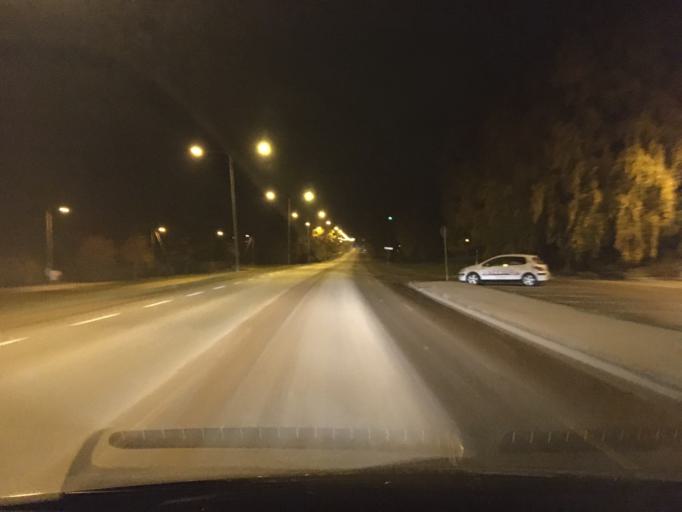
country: EE
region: Tartu
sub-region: Tartu linn
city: Tartu
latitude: 58.4001
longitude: 26.7084
